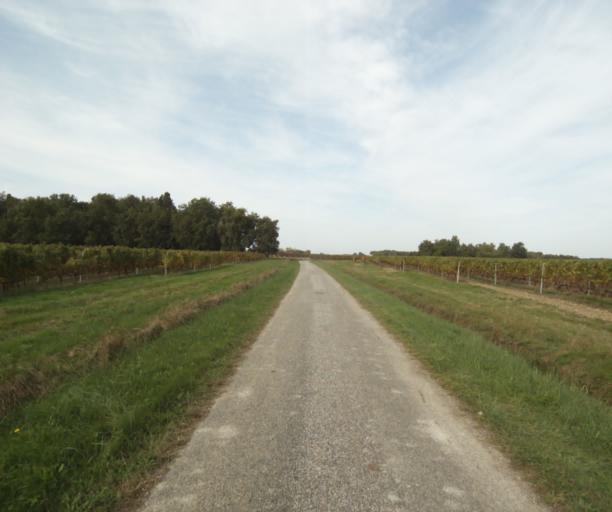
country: FR
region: Midi-Pyrenees
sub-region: Departement du Tarn-et-Garonne
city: Orgueil
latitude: 43.8887
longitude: 1.3950
